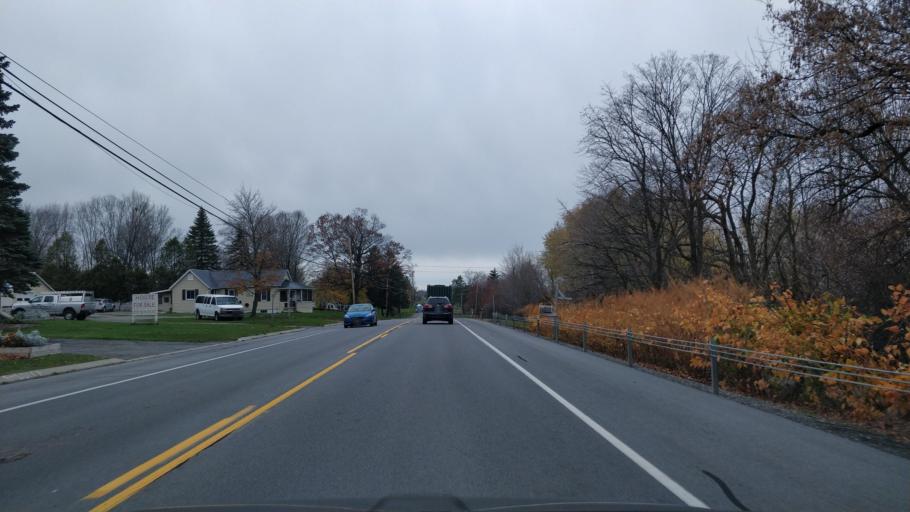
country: CA
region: Ontario
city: Prescott
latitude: 44.6719
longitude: -75.5300
